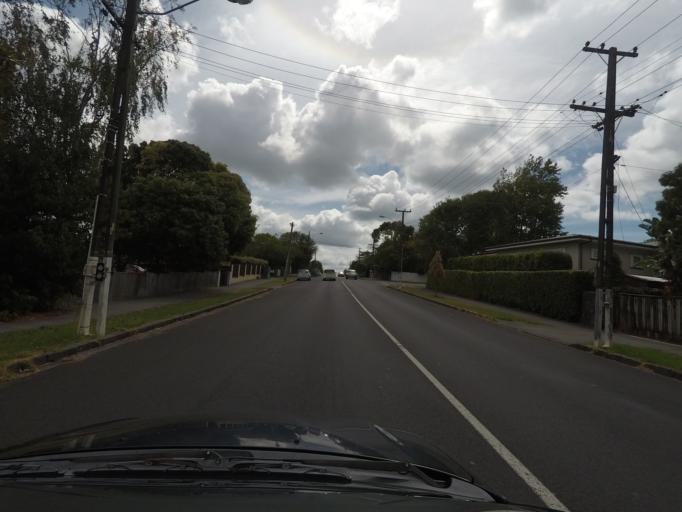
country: NZ
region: Auckland
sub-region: Auckland
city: Rosebank
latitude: -36.8911
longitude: 174.7123
